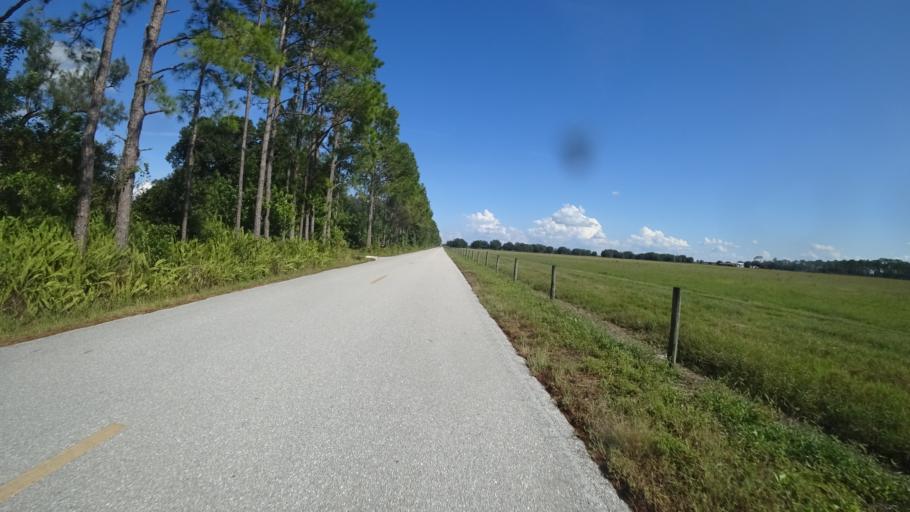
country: US
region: Florida
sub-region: Sarasota County
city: The Meadows
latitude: 27.4308
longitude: -82.3005
